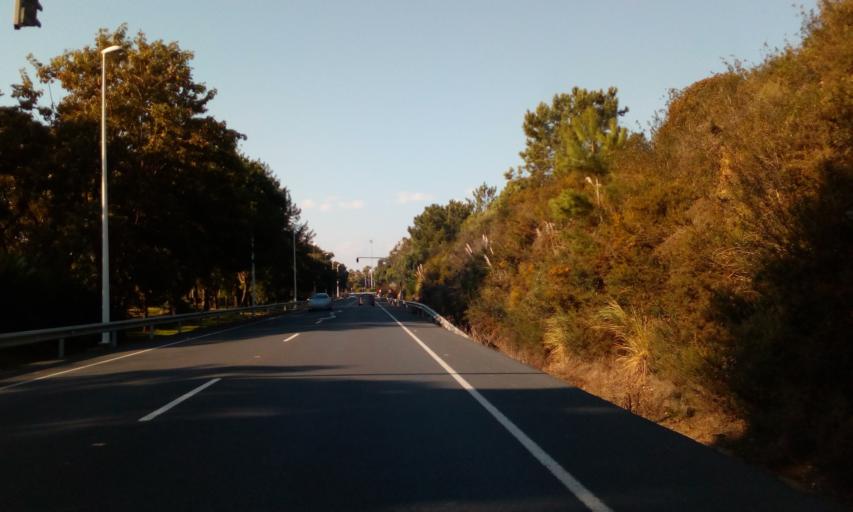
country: ES
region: Andalusia
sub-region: Provincia de Huelva
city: Lepe
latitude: 37.2083
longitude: -7.2328
